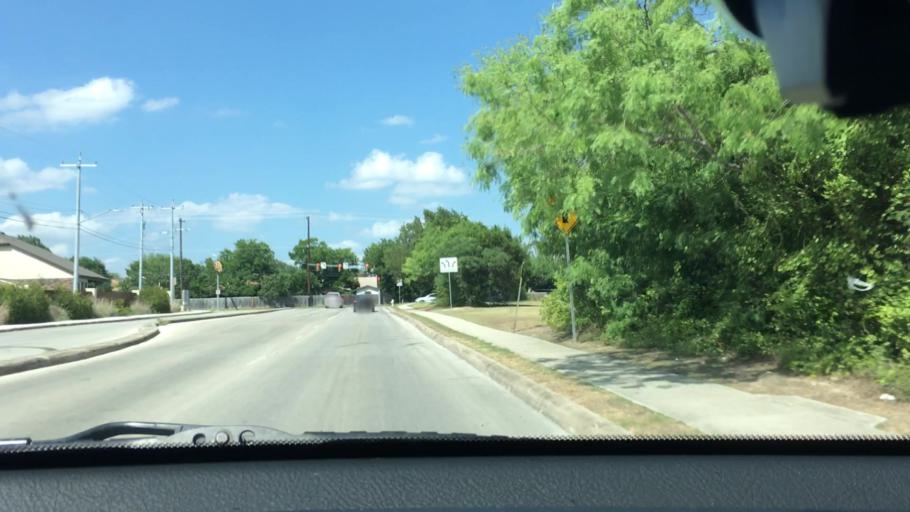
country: US
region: Texas
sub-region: Bexar County
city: Live Oak
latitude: 29.5970
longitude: -98.3856
